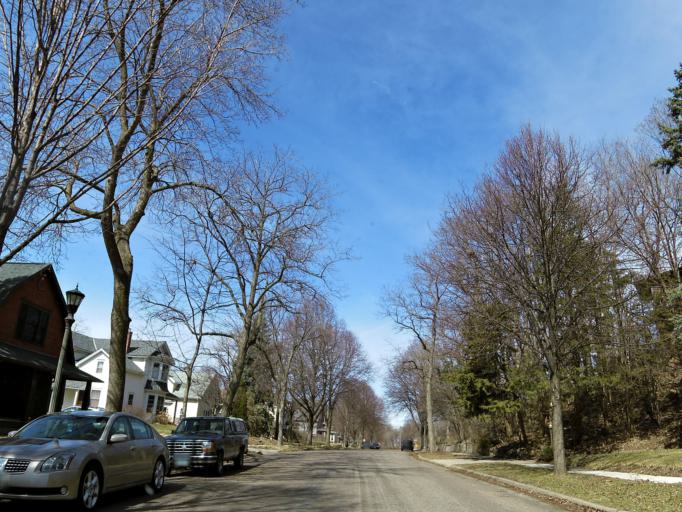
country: US
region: Minnesota
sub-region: Ramsey County
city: Saint Paul
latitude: 44.9493
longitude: -93.0611
